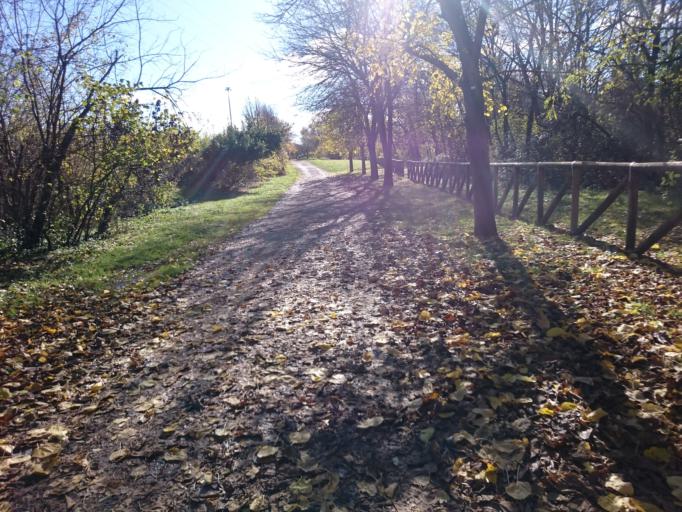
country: IT
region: Emilia-Romagna
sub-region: Provincia di Bologna
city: Bologna
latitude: 44.5160
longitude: 11.3337
